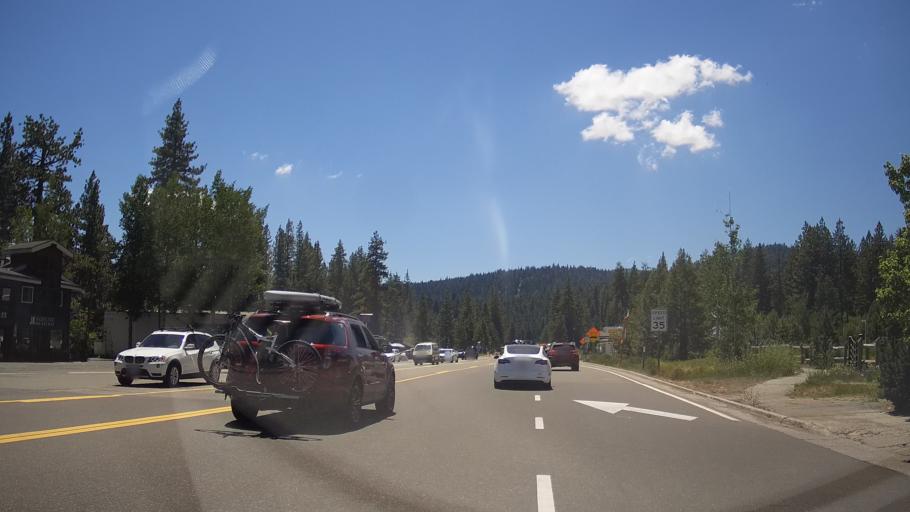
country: US
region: California
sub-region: Placer County
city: Sunnyside-Tahoe City
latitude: 39.1675
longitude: -120.1456
